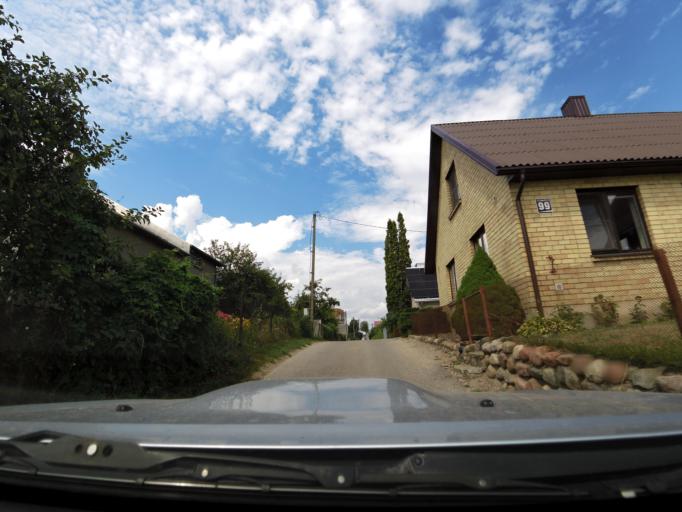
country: LT
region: Taurages apskritis
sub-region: Jurbarkas
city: Jurbarkas
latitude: 55.0780
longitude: 22.7818
